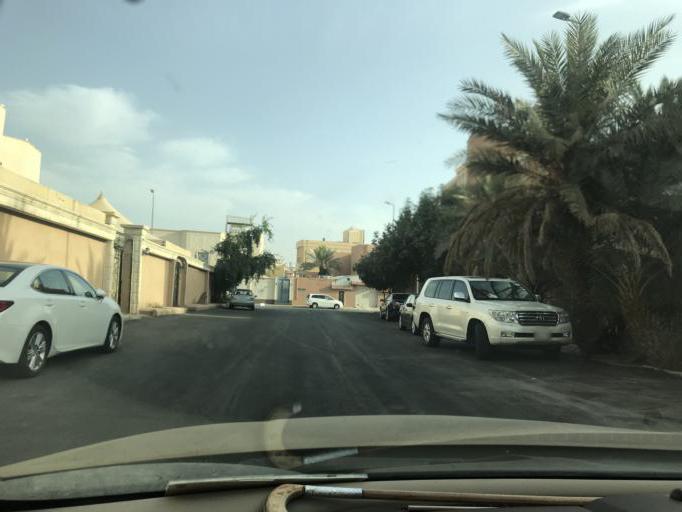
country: SA
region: Ar Riyad
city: Riyadh
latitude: 24.7392
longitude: 46.7505
